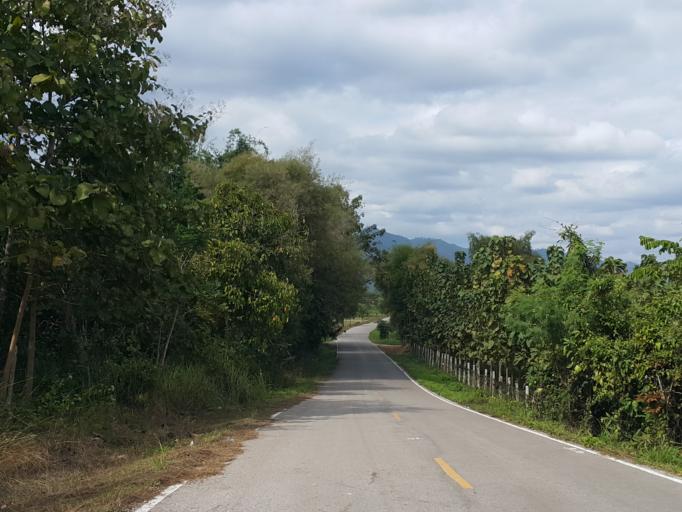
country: TH
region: Lampang
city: Chae Hom
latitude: 18.5501
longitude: 99.4610
